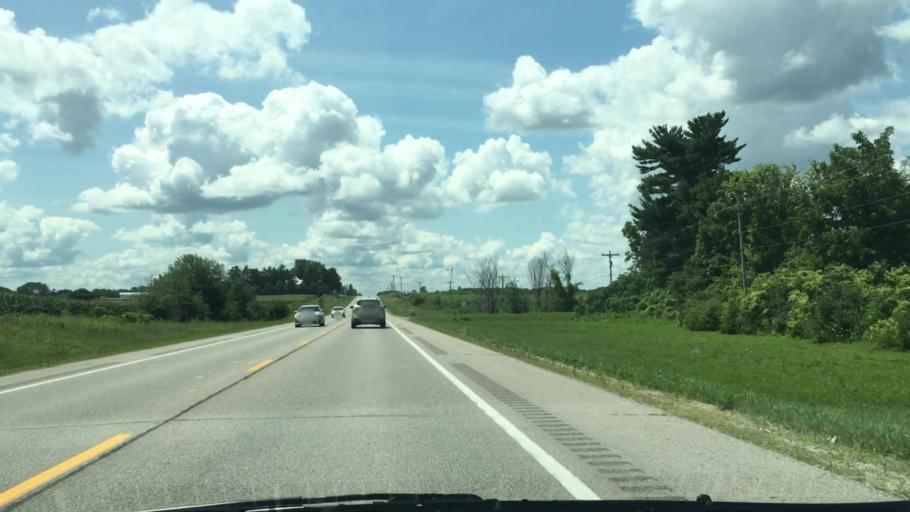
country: US
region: Iowa
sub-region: Johnson County
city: Solon
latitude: 41.7266
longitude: -91.4771
